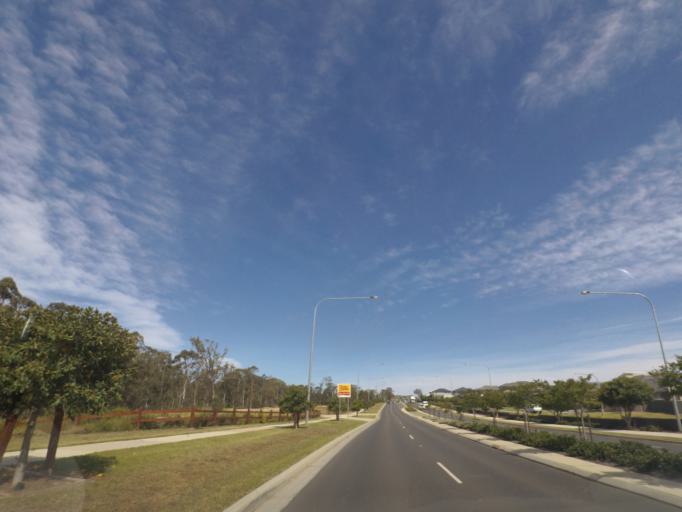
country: AU
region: New South Wales
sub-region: Camden
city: Narellan Vale
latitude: -34.0258
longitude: 150.7841
